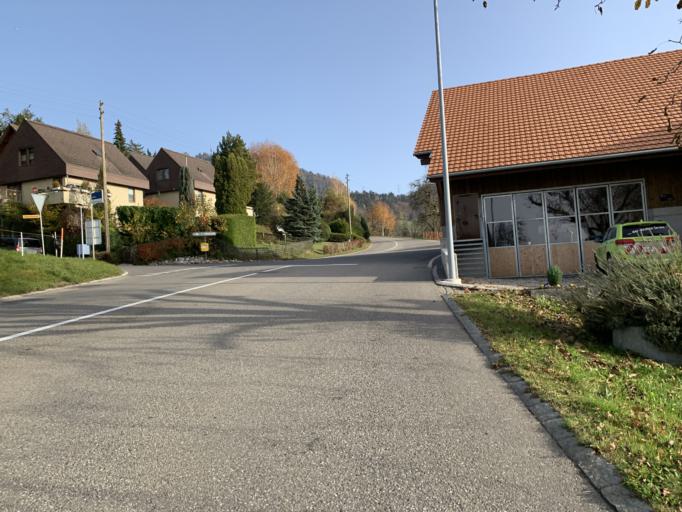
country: CH
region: Zurich
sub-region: Bezirk Hinwil
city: Hadlikon
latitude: 47.2972
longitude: 8.8609
